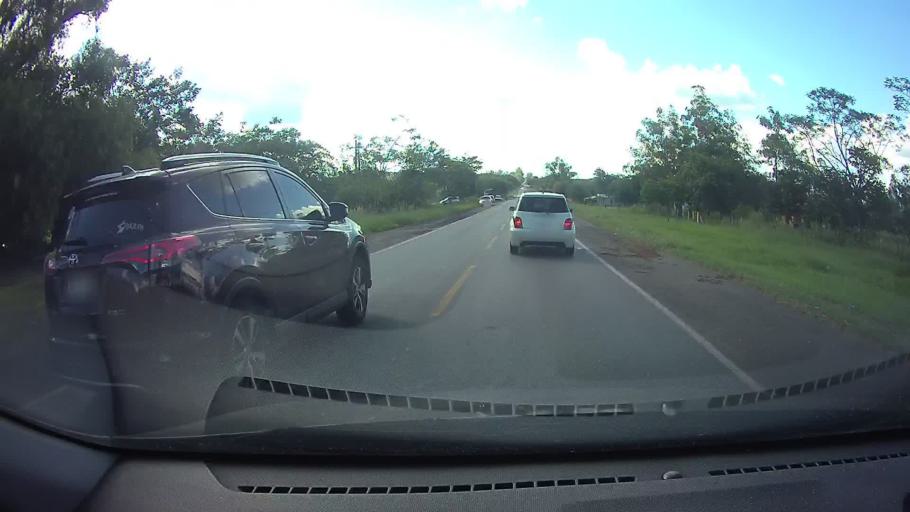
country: PY
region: Cordillera
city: Eusebio Ayala
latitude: -25.4136
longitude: -56.9333
